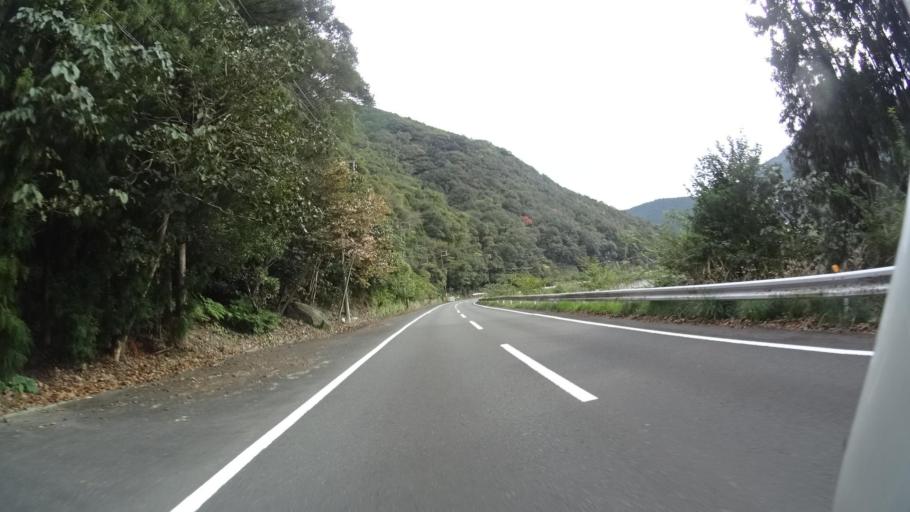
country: JP
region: Wakayama
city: Shingu
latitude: 33.5525
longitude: 135.7009
